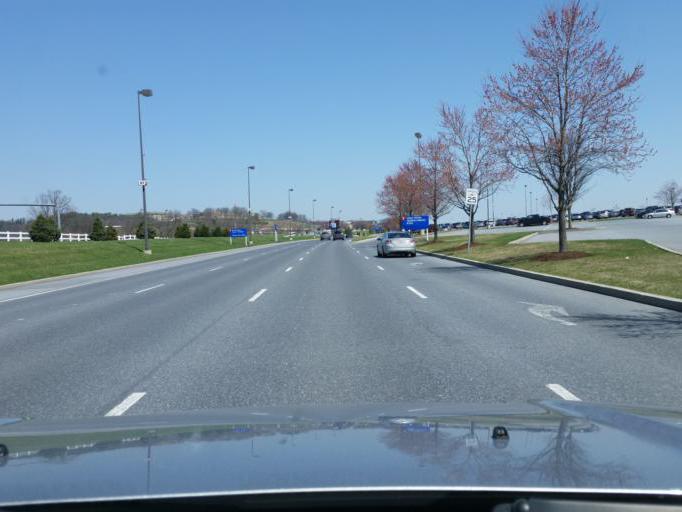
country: US
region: Pennsylvania
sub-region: Dauphin County
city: Hershey
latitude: 40.2868
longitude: -76.6732
